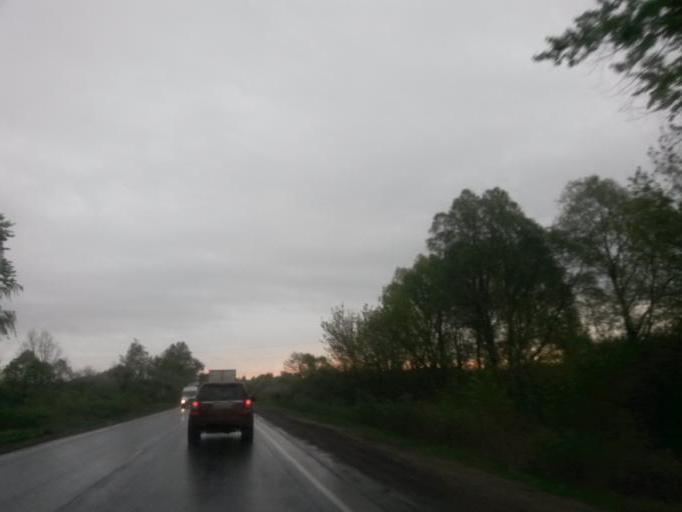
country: RU
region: Moskovskaya
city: Yam
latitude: 55.4592
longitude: 37.6890
